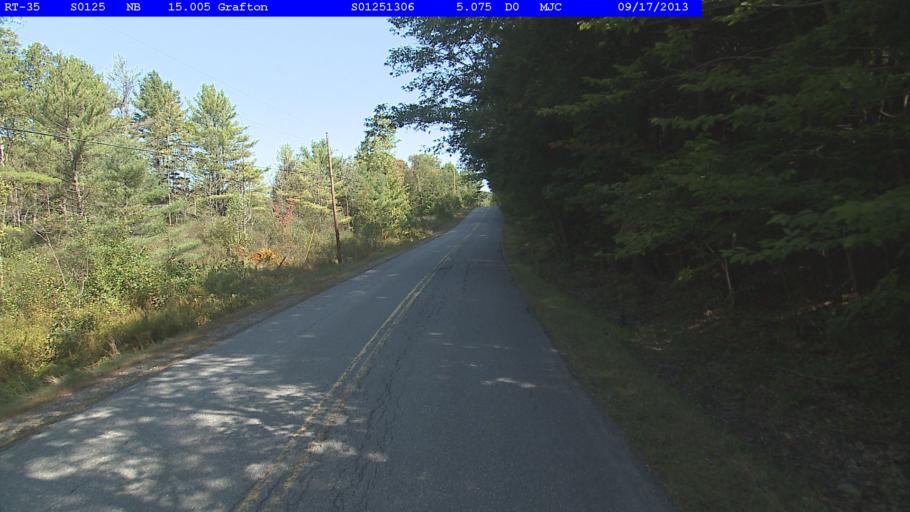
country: US
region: Vermont
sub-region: Windsor County
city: Chester
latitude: 43.1840
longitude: -72.6000
